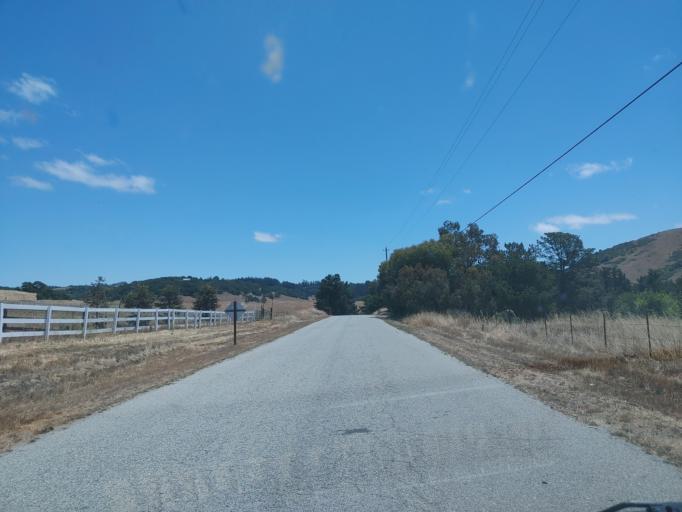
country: US
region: California
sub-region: San Benito County
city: Aromas
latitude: 36.8628
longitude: -121.6287
